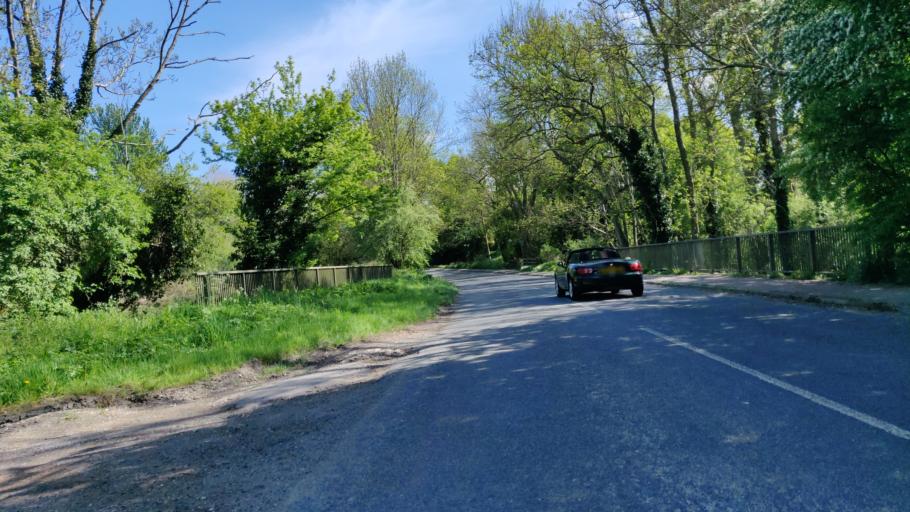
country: GB
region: England
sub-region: West Sussex
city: Rudgwick
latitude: 51.0834
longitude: -0.4555
